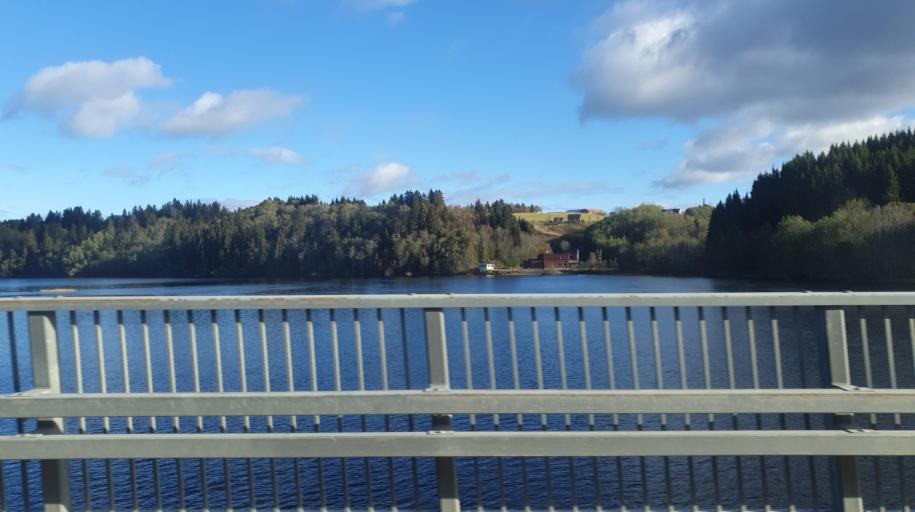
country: NO
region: Sor-Trondelag
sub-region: Klaebu
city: Klaebu
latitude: 63.3108
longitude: 10.4524
